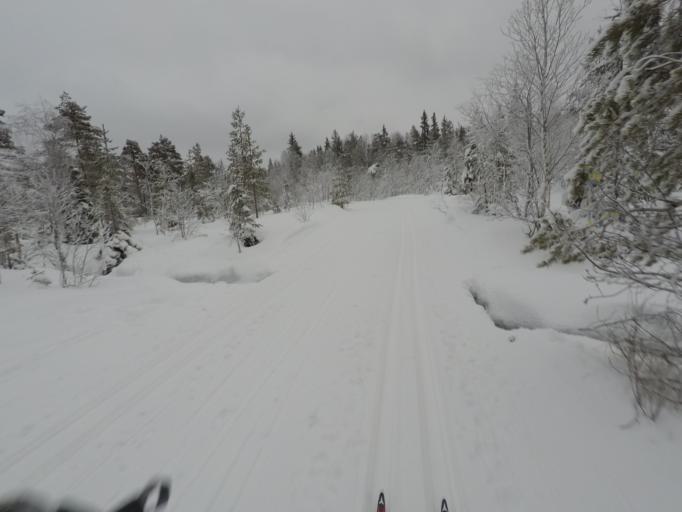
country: SE
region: Vaermland
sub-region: Filipstads Kommun
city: Lesjofors
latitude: 60.1614
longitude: 14.4544
